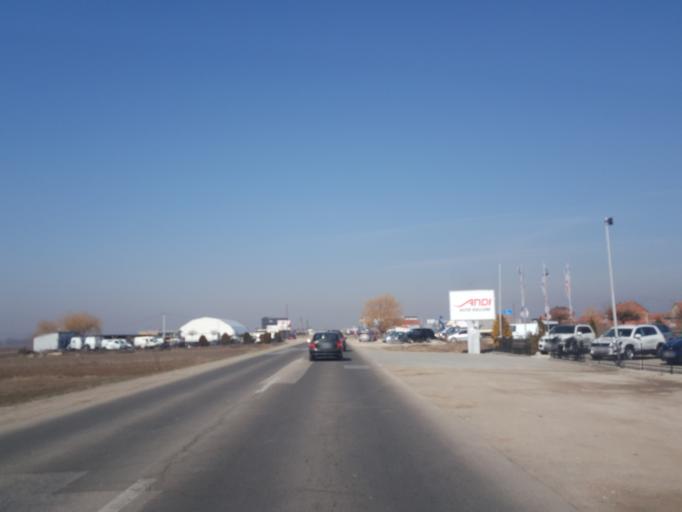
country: XK
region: Mitrovica
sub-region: Vushtrri
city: Vushtrri
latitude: 42.7650
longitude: 21.0264
